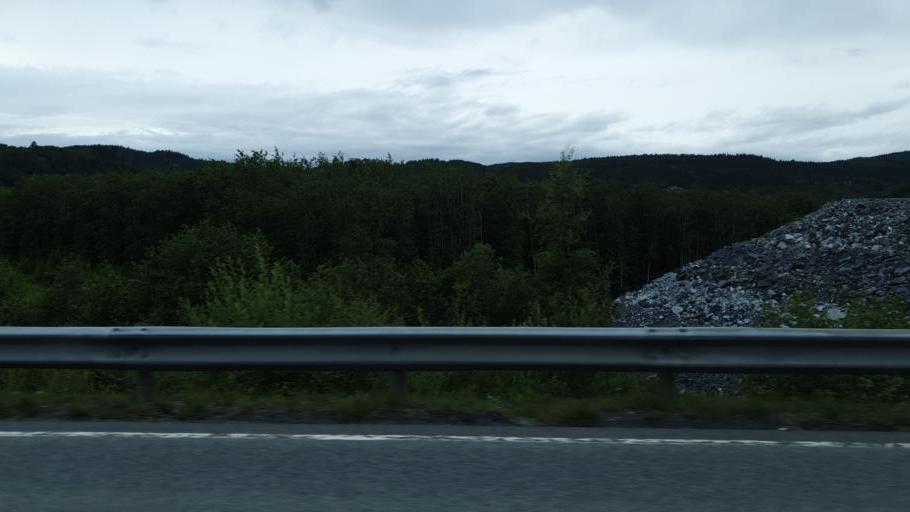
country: NO
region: Sor-Trondelag
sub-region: Melhus
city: Lundamo
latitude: 63.1049
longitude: 10.2357
